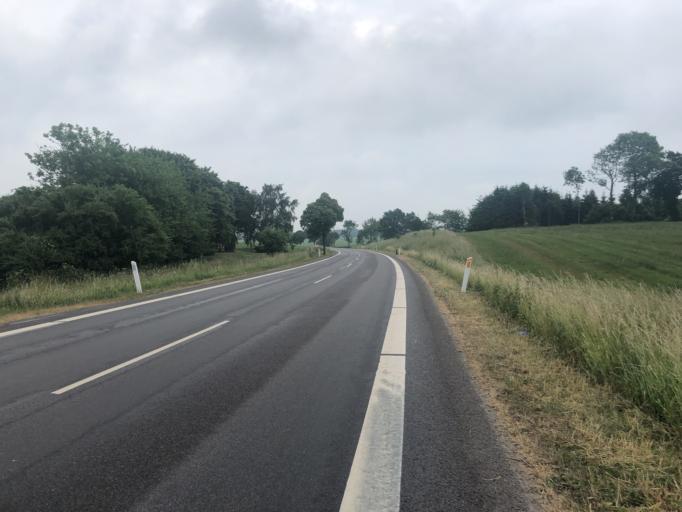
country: DK
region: Capital Region
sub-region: Bornholm Kommune
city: Akirkeby
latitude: 55.1520
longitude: 14.9019
